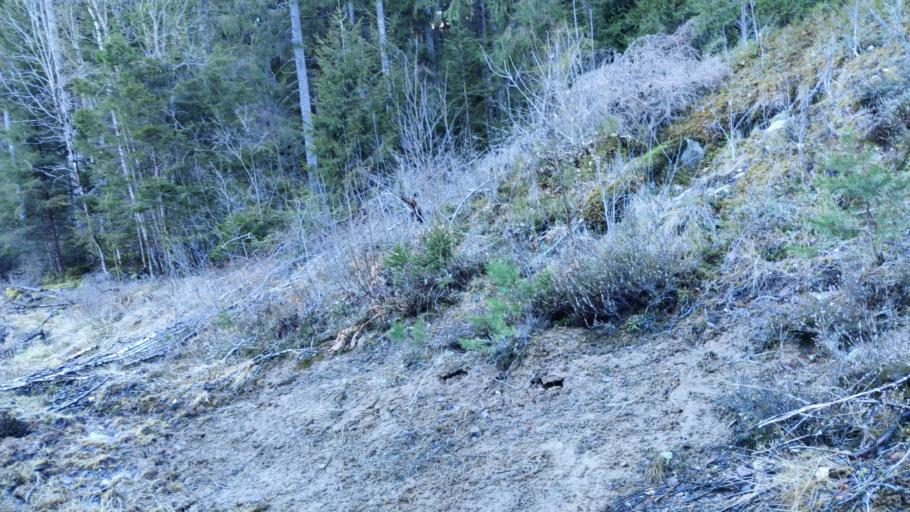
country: SE
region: Vaestra Goetaland
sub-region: Uddevalla Kommun
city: Uddevalla
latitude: 58.3494
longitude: 11.9680
